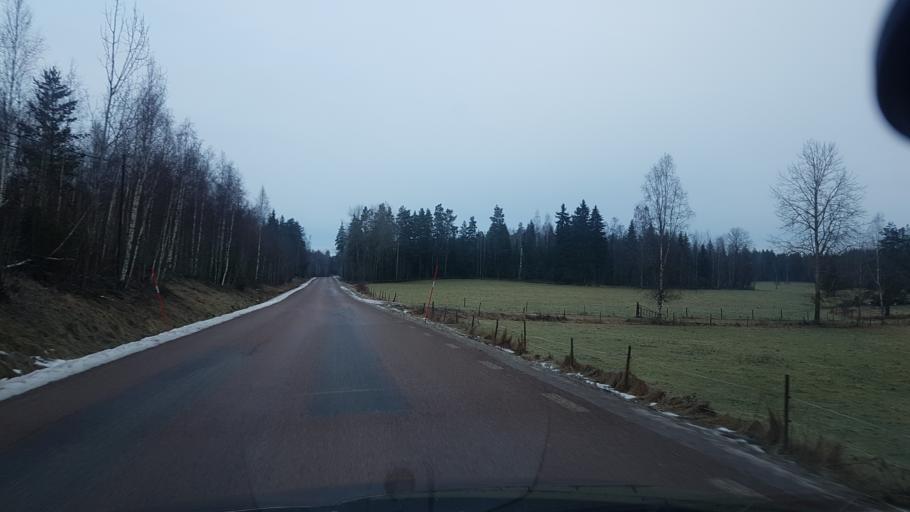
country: SE
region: Dalarna
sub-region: Borlange Kommun
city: Ornas
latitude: 60.4574
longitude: 15.6166
